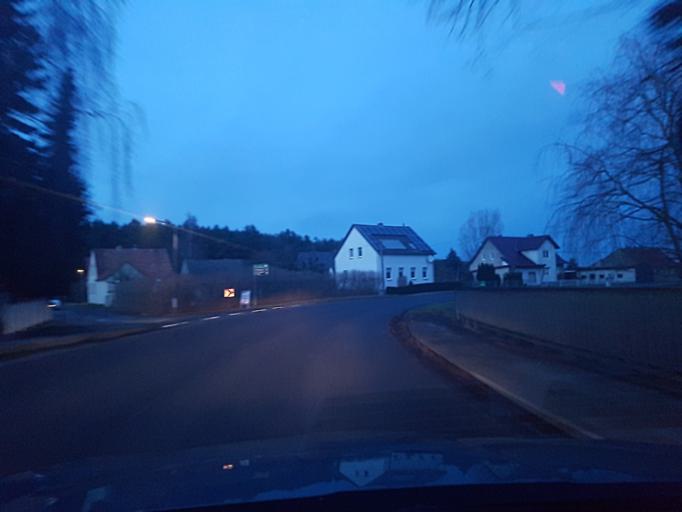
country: DE
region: Brandenburg
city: Bad Liebenwerda
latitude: 51.5390
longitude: 13.4088
